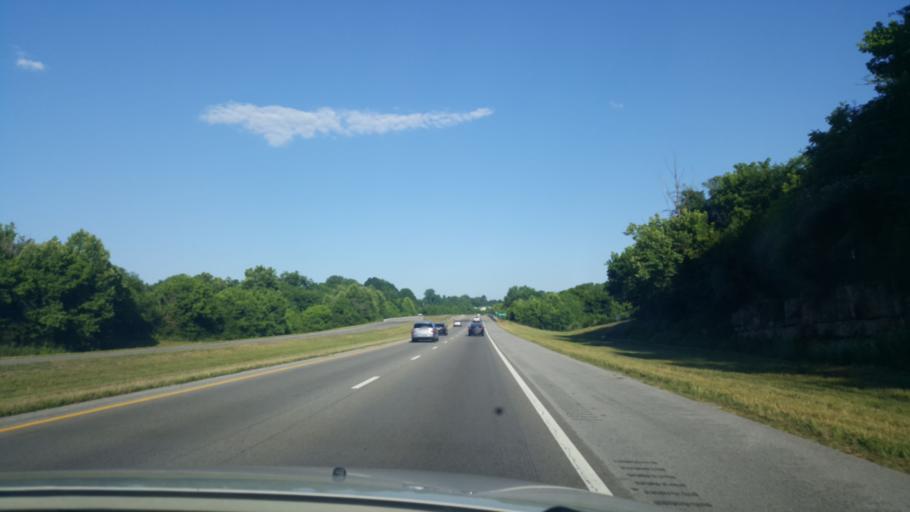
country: US
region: Tennessee
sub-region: Maury County
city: Columbia
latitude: 35.6376
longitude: -87.0317
